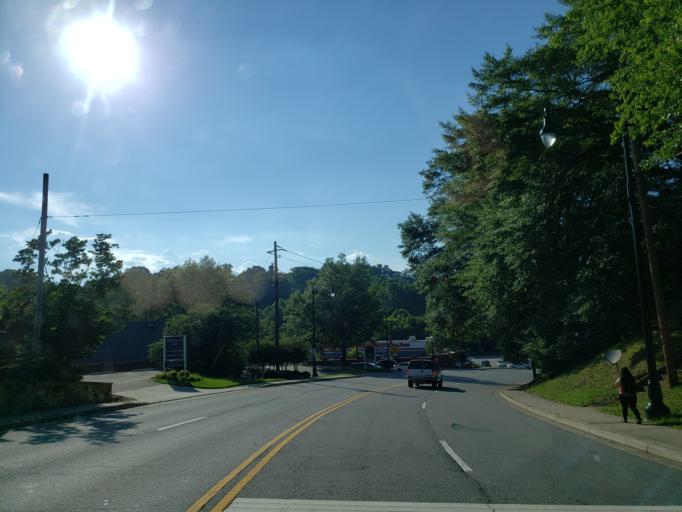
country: US
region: Georgia
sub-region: Cherokee County
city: Canton
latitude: 34.2376
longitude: -84.4941
